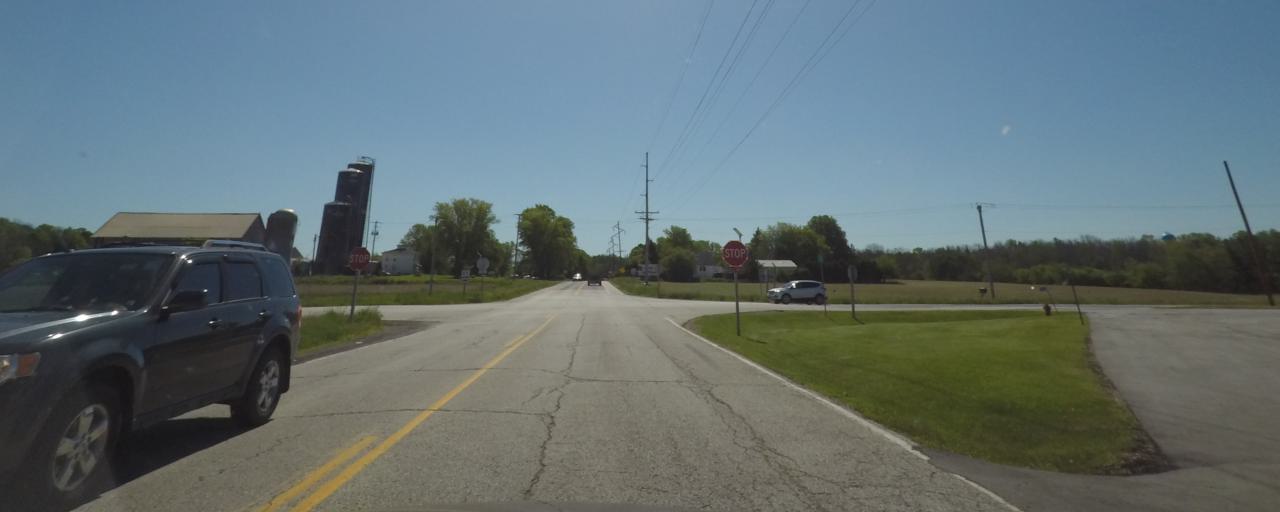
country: US
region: Wisconsin
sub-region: Sheboygan County
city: Sheboygan Falls
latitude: 43.7397
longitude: -87.8508
